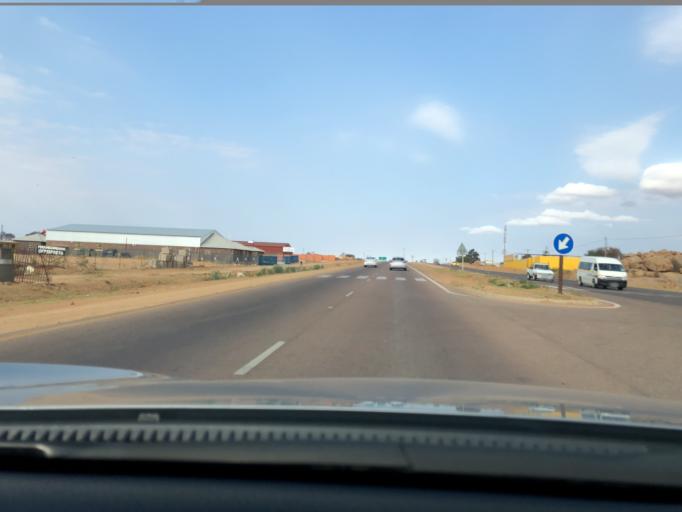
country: ZA
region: Limpopo
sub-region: Capricorn District Municipality
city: Mankoeng
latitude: -23.8905
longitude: 29.6620
